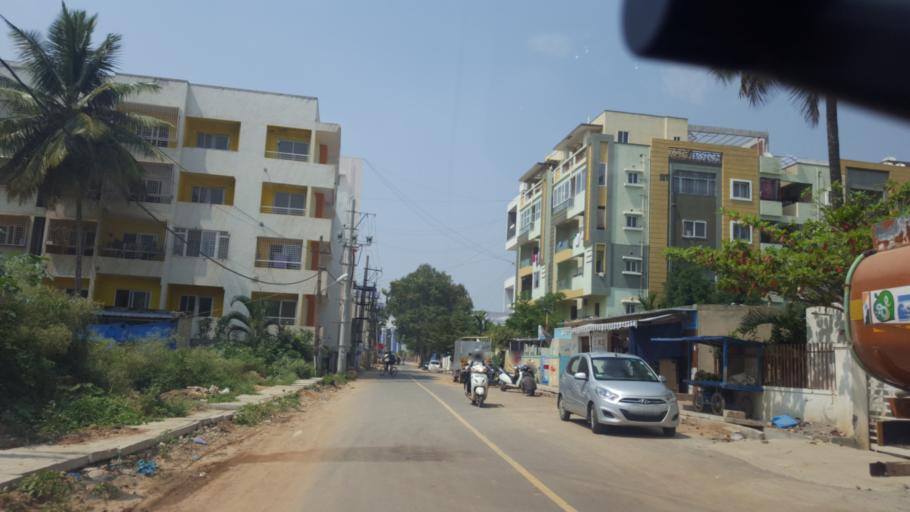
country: IN
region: Karnataka
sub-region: Bangalore Urban
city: Bangalore
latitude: 12.9413
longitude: 77.7032
